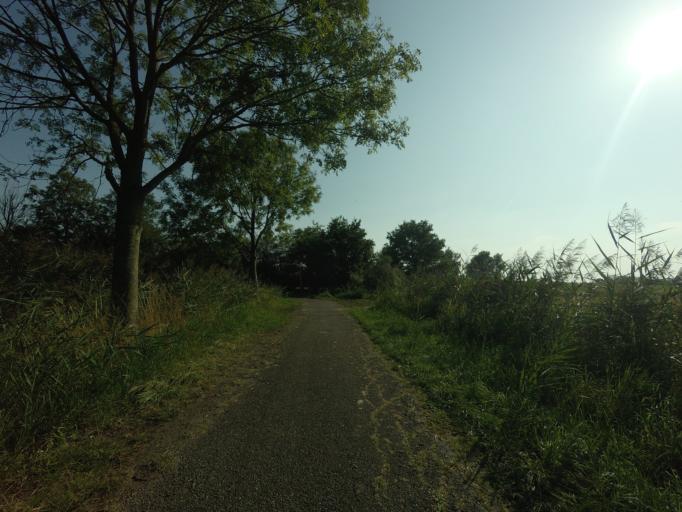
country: NL
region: Groningen
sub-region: Gemeente Zuidhorn
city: Aduard
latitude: 53.1974
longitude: 6.4455
